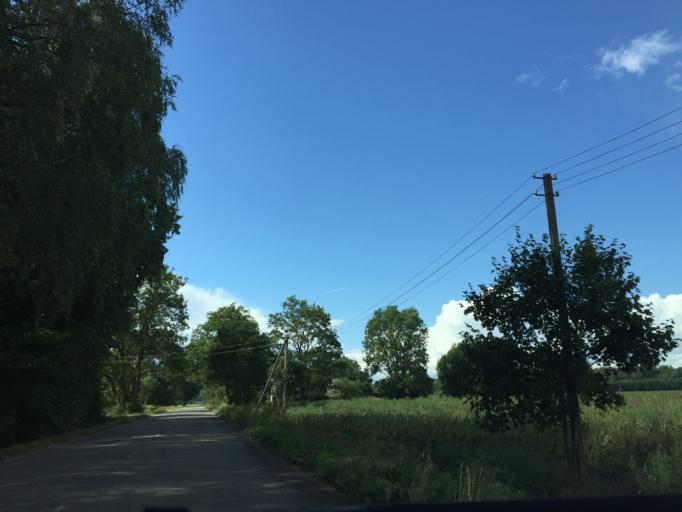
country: LT
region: Siauliu apskritis
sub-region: Joniskis
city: Joniskis
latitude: 56.3291
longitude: 23.5714
